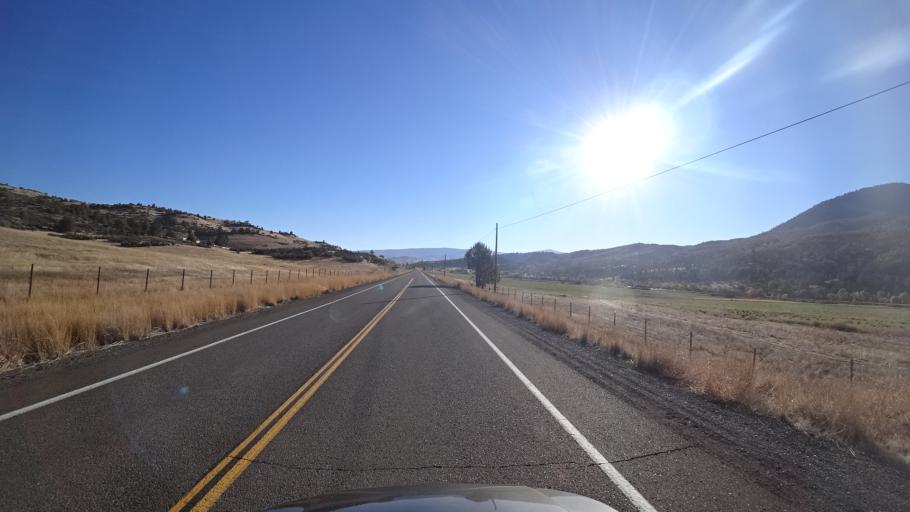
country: US
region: California
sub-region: Siskiyou County
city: Montague
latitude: 41.8976
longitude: -122.5350
